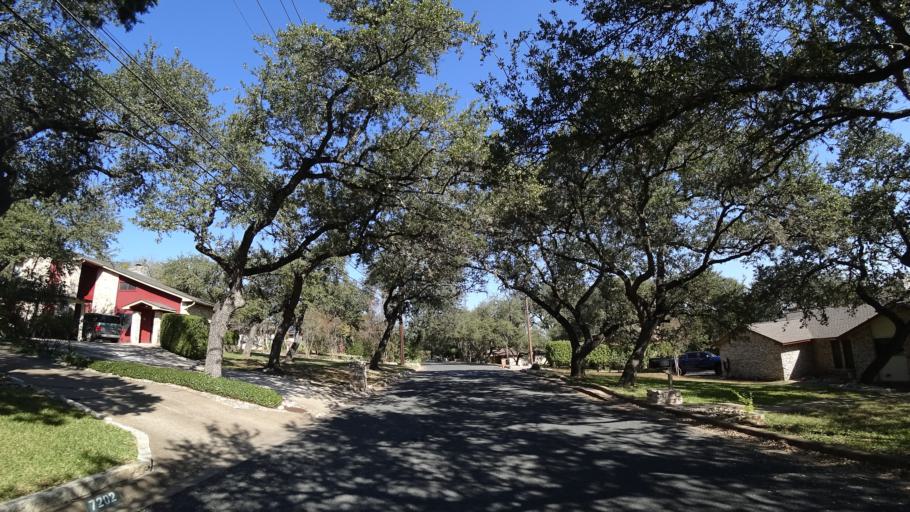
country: US
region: Texas
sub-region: Travis County
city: Barton Creek
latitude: 30.2291
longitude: -97.8707
